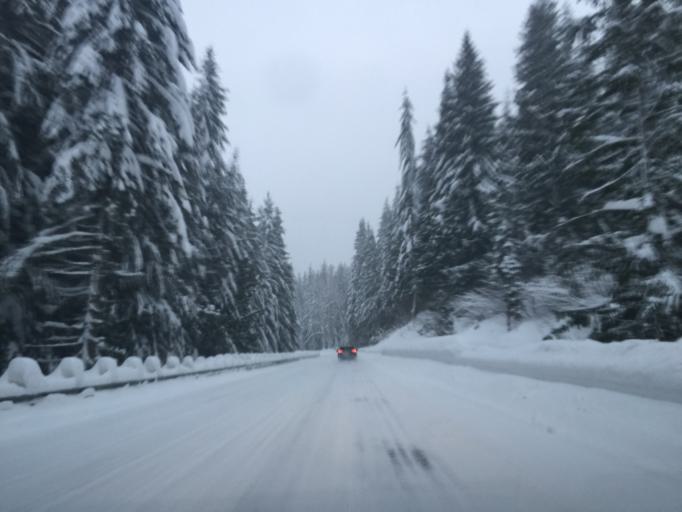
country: US
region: Washington
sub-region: Chelan County
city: Leavenworth
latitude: 47.7785
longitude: -121.0242
